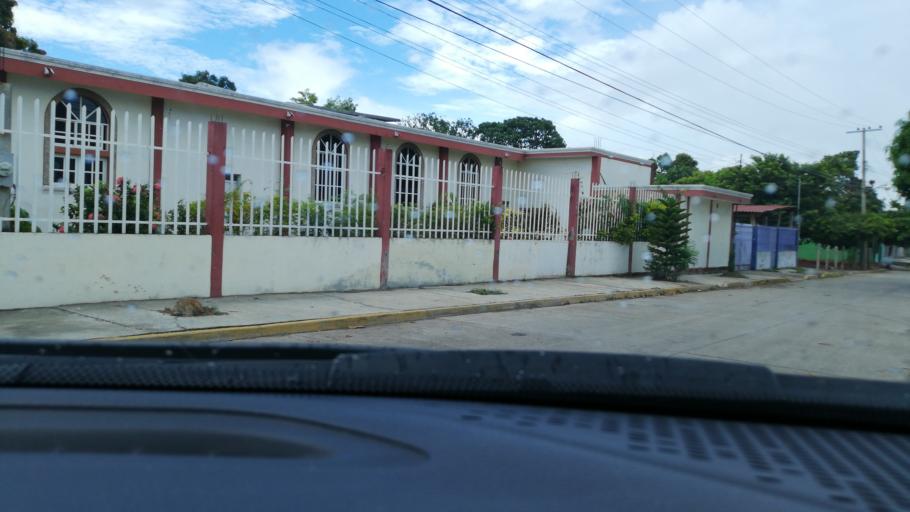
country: MX
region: Oaxaca
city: Asuncion Ixtaltepec
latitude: 16.5088
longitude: -95.0500
